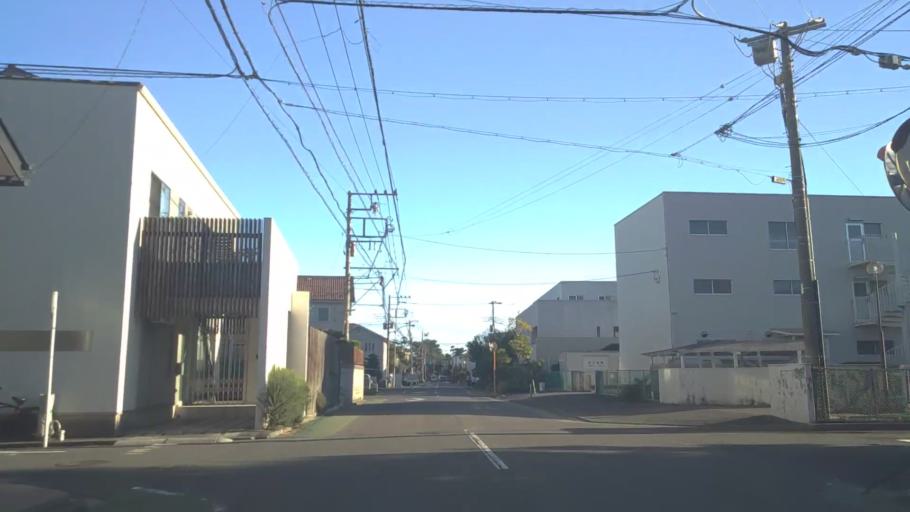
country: JP
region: Kanagawa
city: Chigasaki
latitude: 35.3244
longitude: 139.4150
